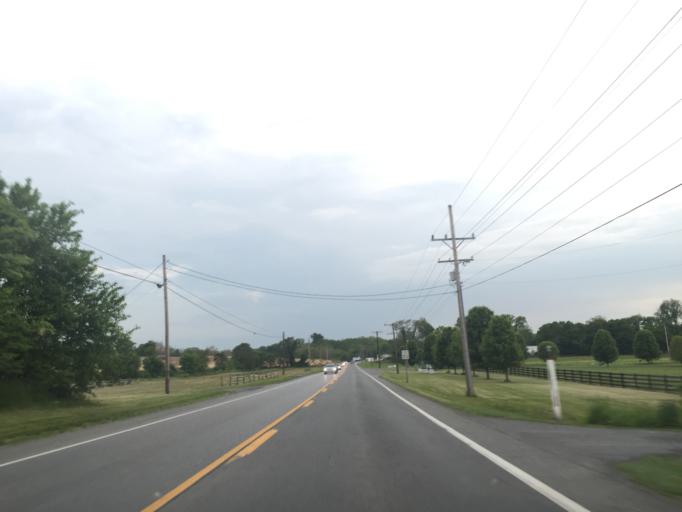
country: US
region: West Virginia
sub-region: Jefferson County
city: Charles Town
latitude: 39.2416
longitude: -77.8965
